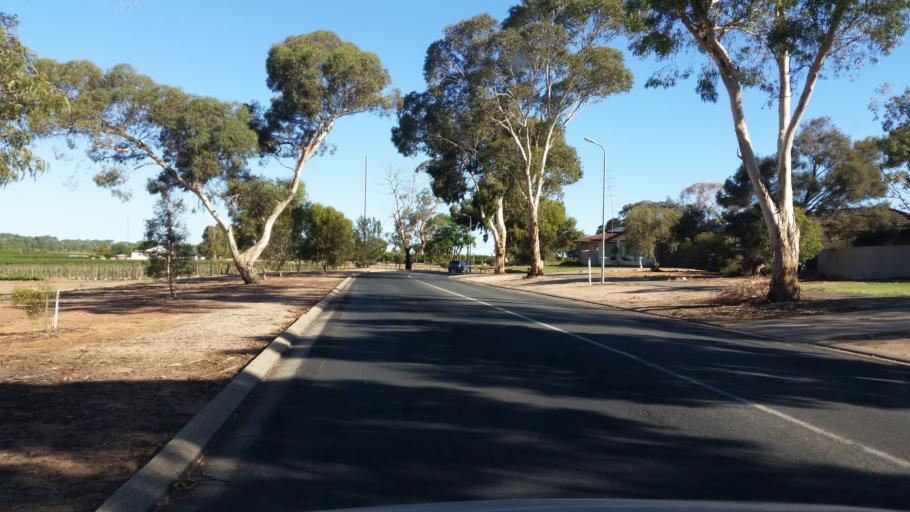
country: AU
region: South Australia
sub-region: Loxton Waikerie
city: Waikerie
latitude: -34.1880
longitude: 139.9857
